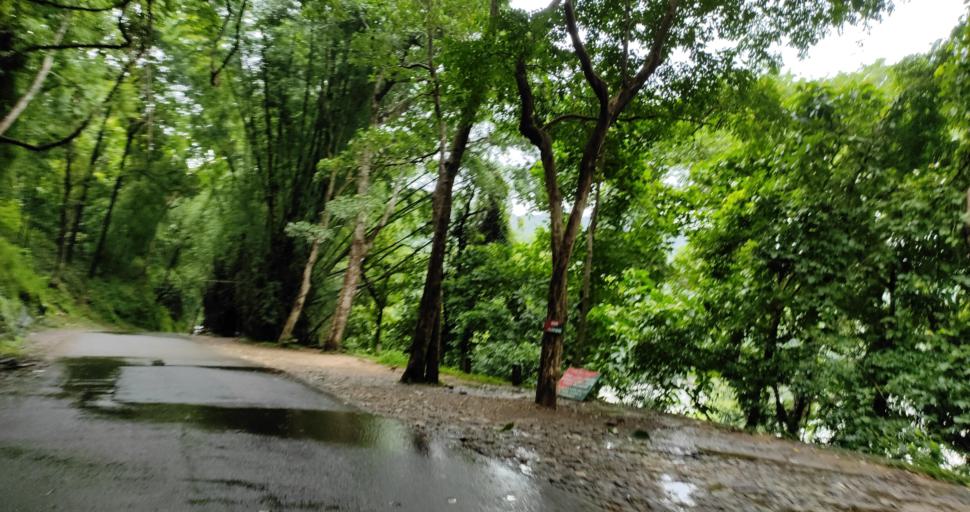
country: IN
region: Kerala
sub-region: Ernakulam
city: Angamali
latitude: 10.2923
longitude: 76.5657
